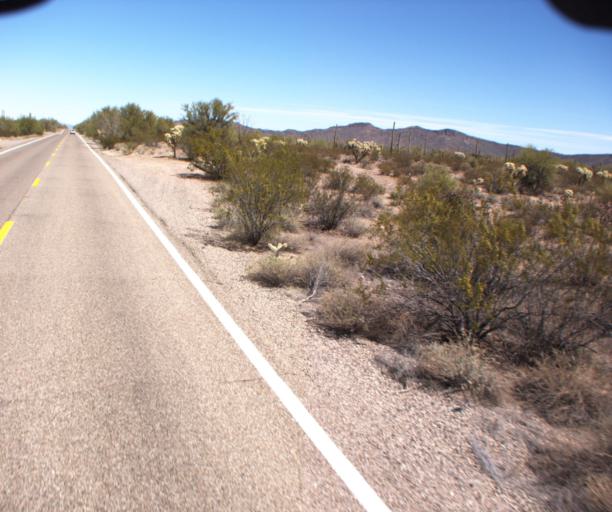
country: US
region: Arizona
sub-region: Pima County
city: Ajo
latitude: 32.1615
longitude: -112.7640
